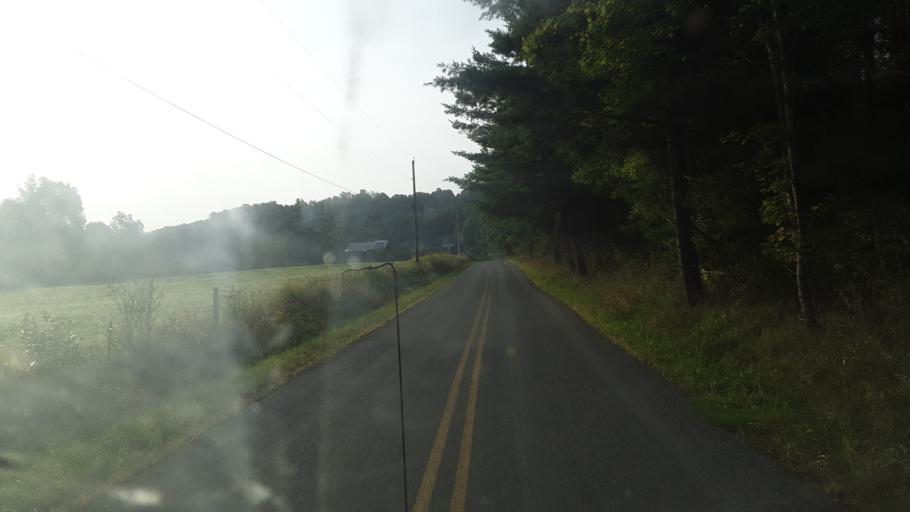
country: US
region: Pennsylvania
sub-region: Jefferson County
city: Punxsutawney
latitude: 40.9561
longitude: -79.1459
